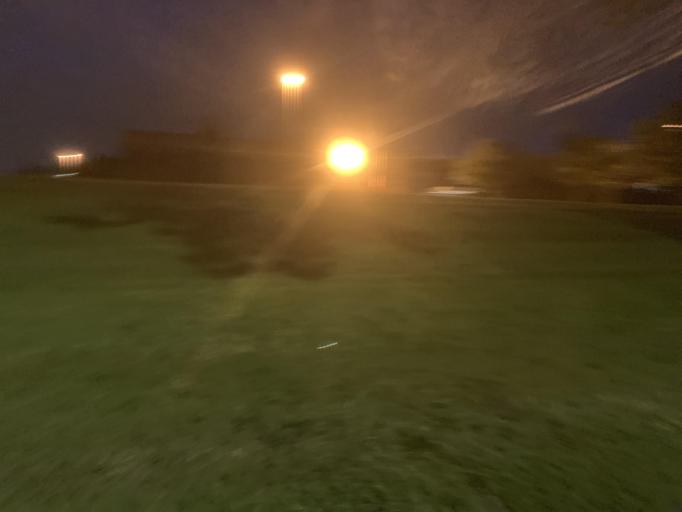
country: US
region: Nebraska
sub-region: Douglas County
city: Ralston
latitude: 41.1890
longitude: -96.0880
